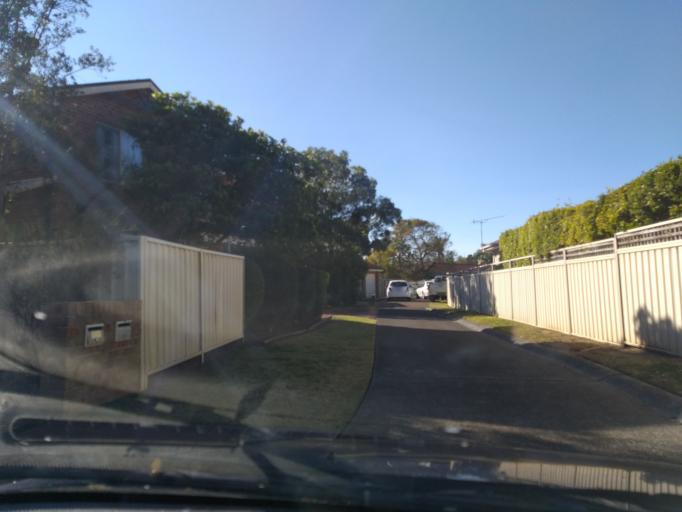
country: AU
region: New South Wales
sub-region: Wollongong
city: Mount Saint Thomas
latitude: -34.4437
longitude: 150.8587
